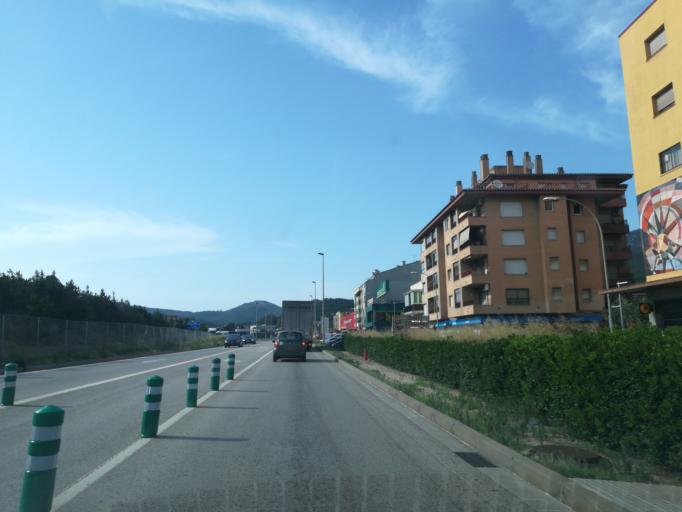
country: ES
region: Catalonia
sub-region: Provincia de Girona
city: la Jonquera
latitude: 42.4198
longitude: 2.8710
